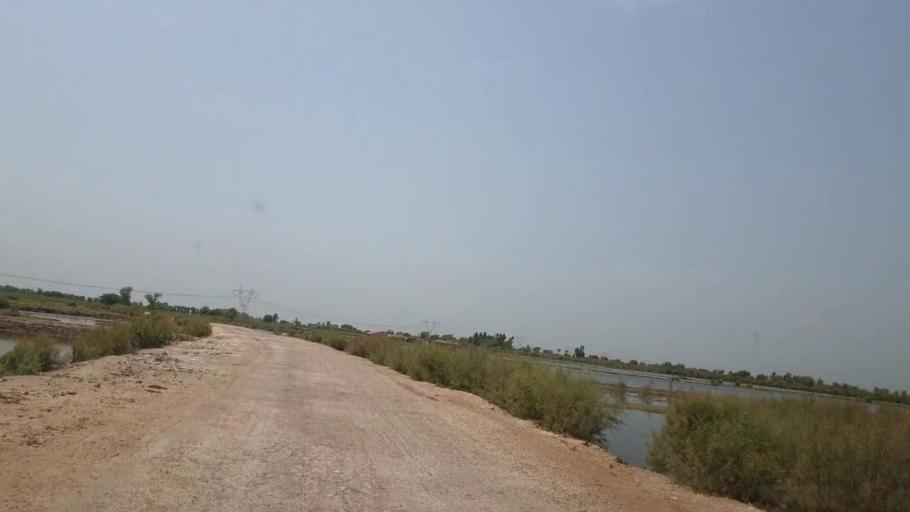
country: PK
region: Sindh
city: Shikarpur
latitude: 27.8937
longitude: 68.6311
